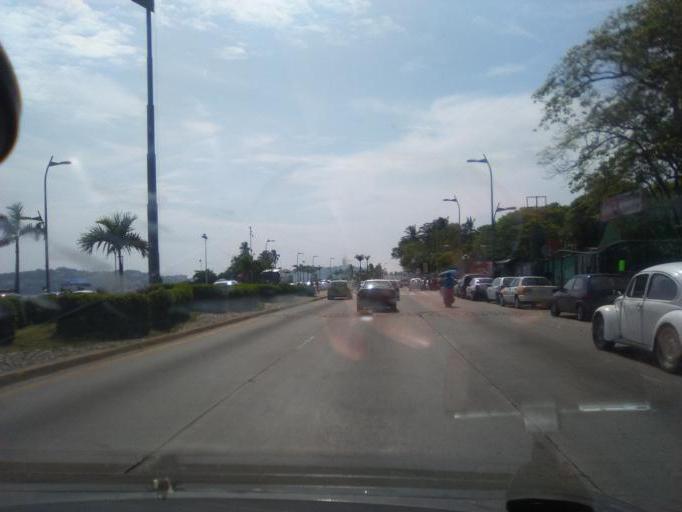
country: MX
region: Guerrero
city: Acapulco de Juarez
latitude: 16.8594
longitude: -99.8865
